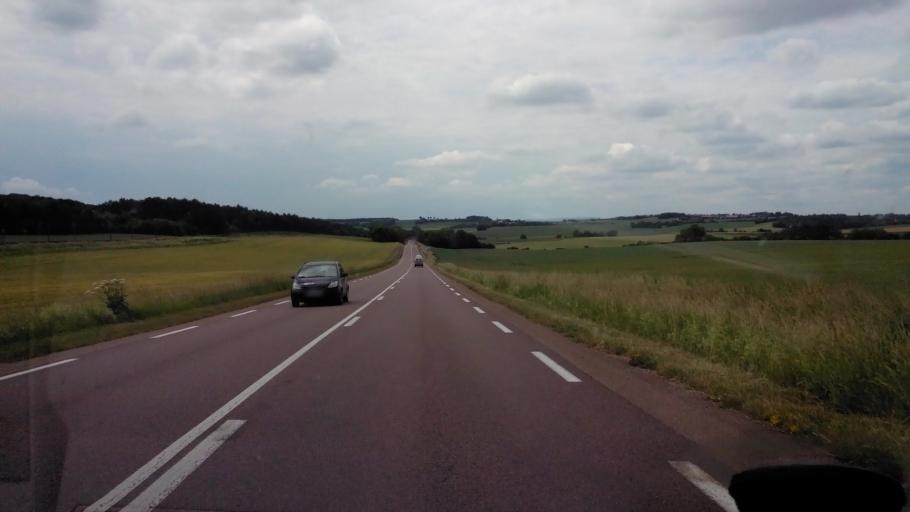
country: FR
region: Bourgogne
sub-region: Departement de la Cote-d'Or
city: Marcilly-sur-Tille
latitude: 47.4607
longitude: 5.1329
